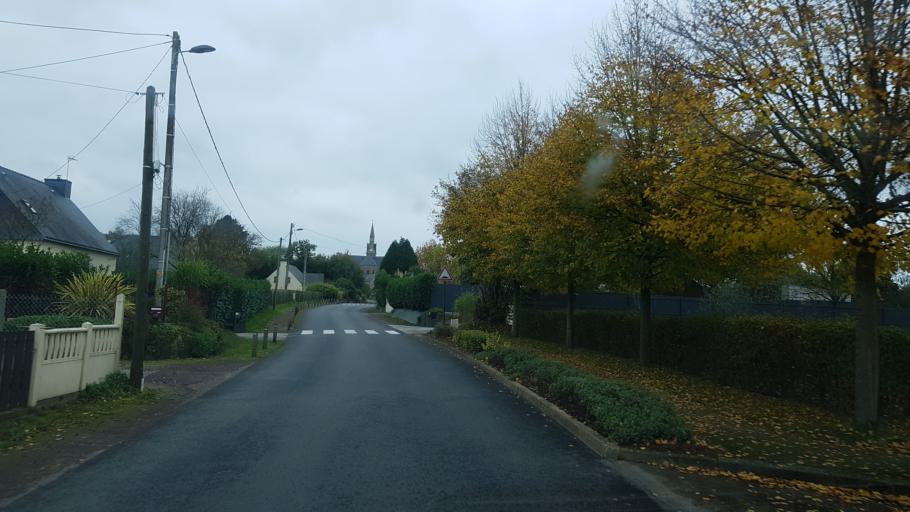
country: FR
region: Brittany
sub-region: Departement du Morbihan
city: Serent
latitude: 47.7816
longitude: -2.5081
